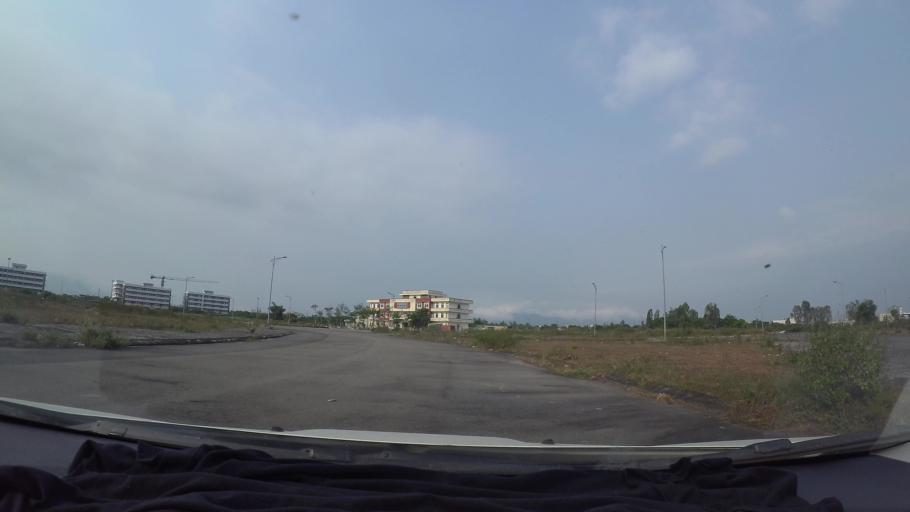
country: VN
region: Da Nang
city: Lien Chieu
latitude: 16.0457
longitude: 108.1601
